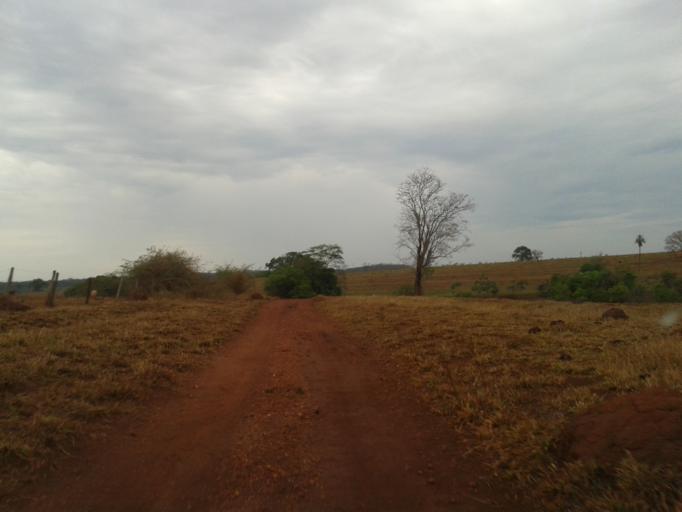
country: BR
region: Minas Gerais
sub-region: Santa Vitoria
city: Santa Vitoria
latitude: -18.8610
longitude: -49.8265
